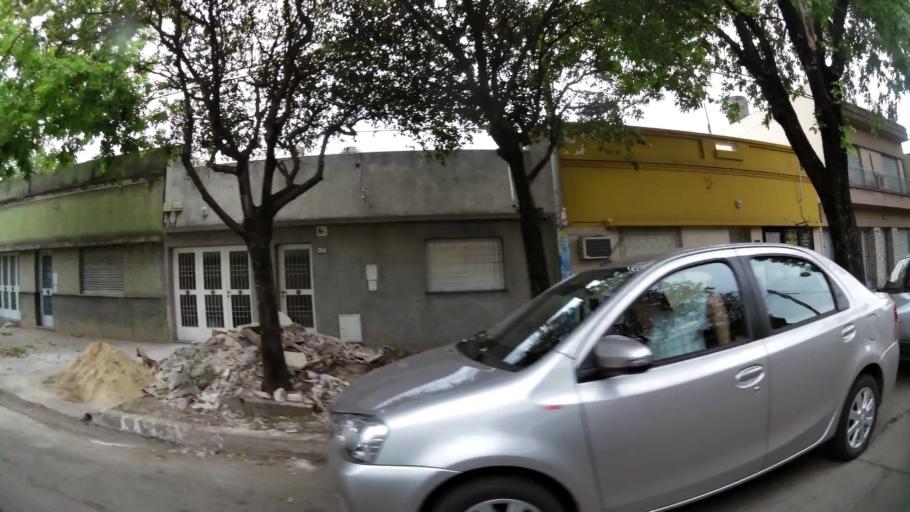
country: AR
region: Santa Fe
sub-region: Departamento de Rosario
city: Rosario
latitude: -32.9878
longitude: -60.6530
